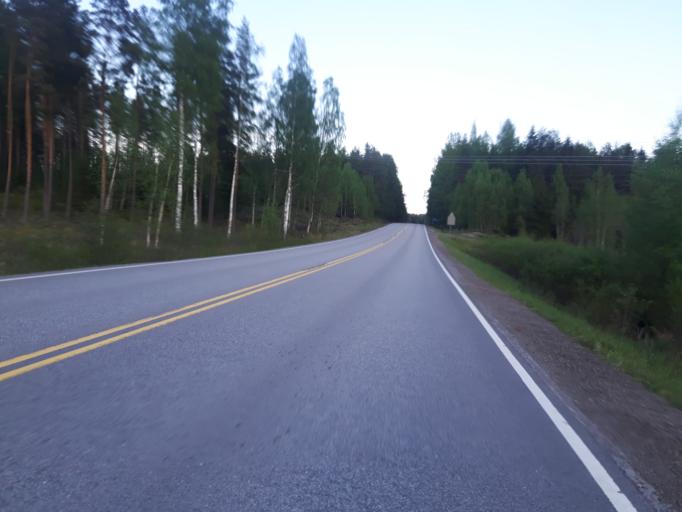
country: FI
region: Uusimaa
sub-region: Loviisa
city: Perna
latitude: 60.4553
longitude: 26.0878
